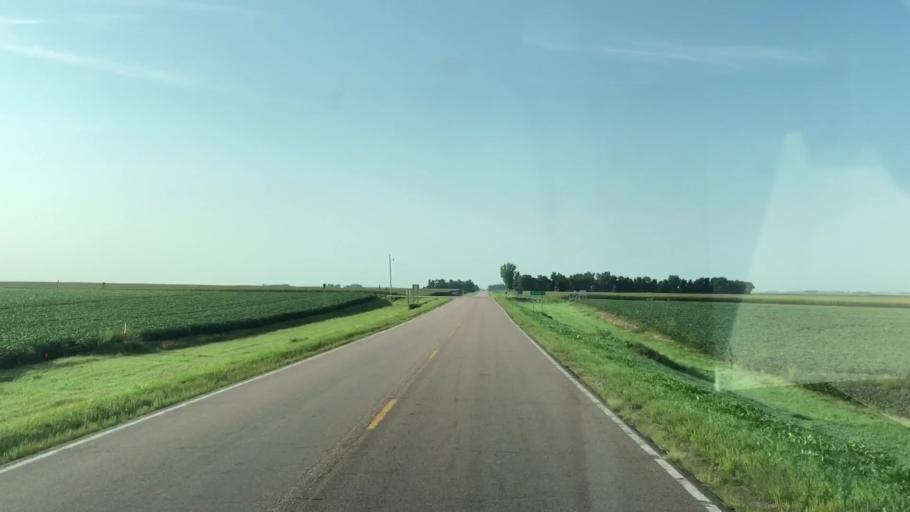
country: US
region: Iowa
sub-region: Lyon County
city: George
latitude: 43.3185
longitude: -95.9989
